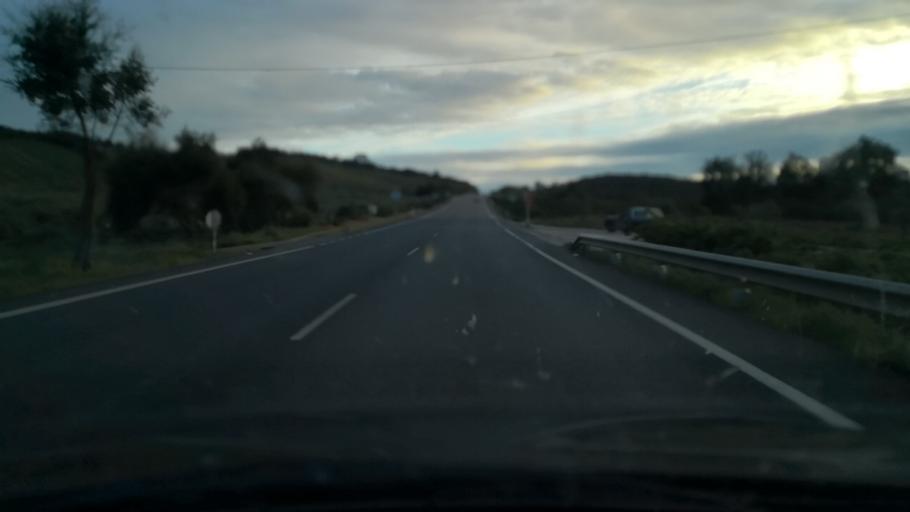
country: ES
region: Extremadura
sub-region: Provincia de Badajoz
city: Puebla de Obando
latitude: 39.1711
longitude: -6.6269
